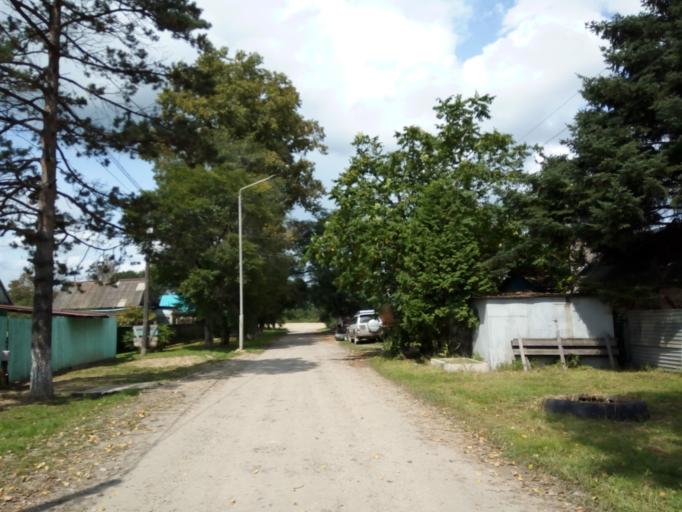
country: RU
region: Primorskiy
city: Dal'nerechensk
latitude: 45.9550
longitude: 133.8166
